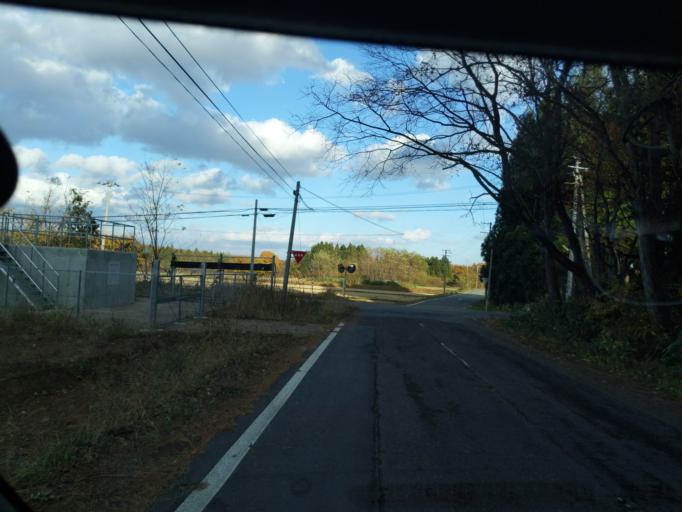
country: JP
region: Iwate
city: Mizusawa
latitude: 39.1202
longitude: 140.9866
